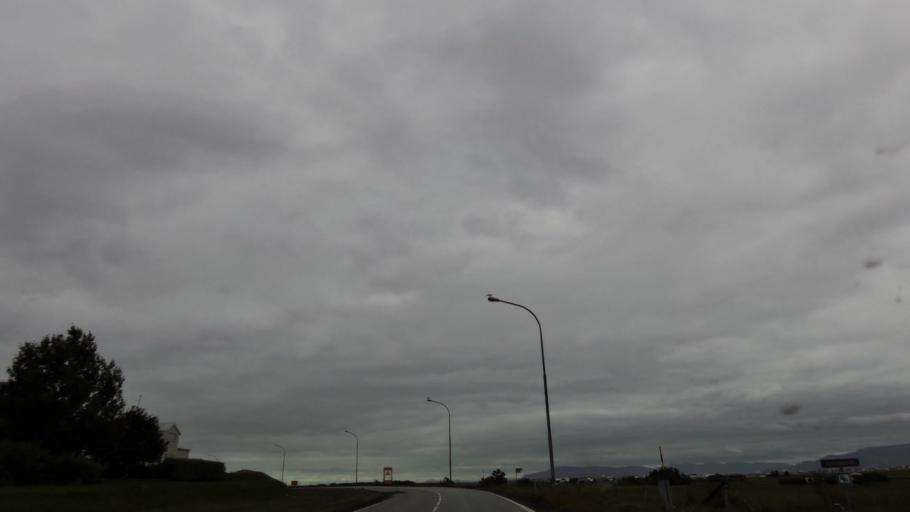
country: IS
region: Capital Region
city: Alftanes
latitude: 64.1070
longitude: -22.0094
